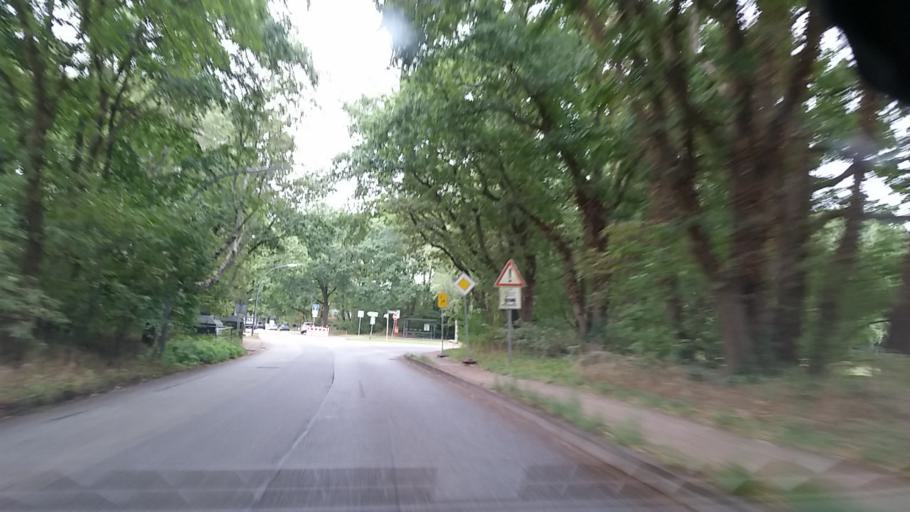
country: DE
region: Schleswig-Holstein
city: Wedel
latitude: 53.5709
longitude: 9.7414
